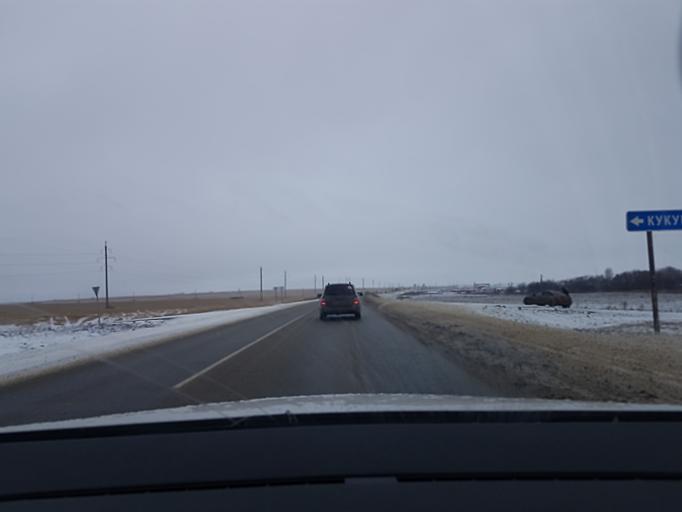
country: RU
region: Rjazan
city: Vilenka
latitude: 54.3325
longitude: 38.8029
